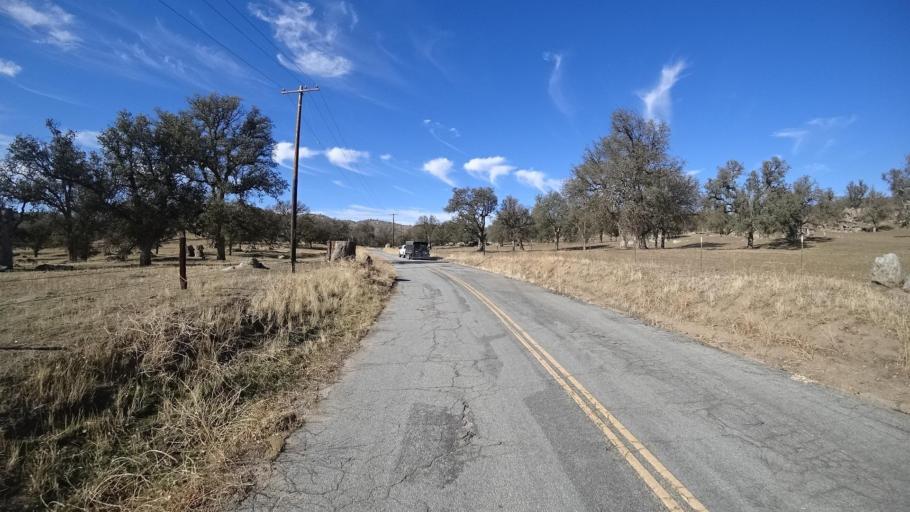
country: US
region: California
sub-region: Kern County
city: Alta Sierra
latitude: 35.6209
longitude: -118.7373
